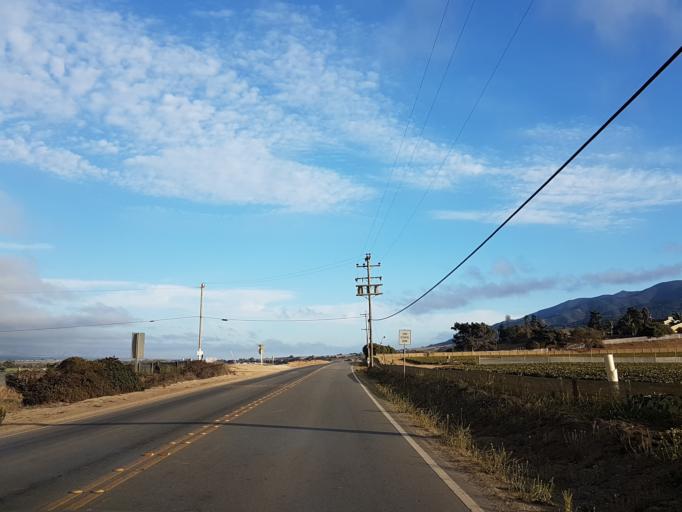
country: US
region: California
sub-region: Monterey County
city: Chualar
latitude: 36.5889
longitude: -121.6044
